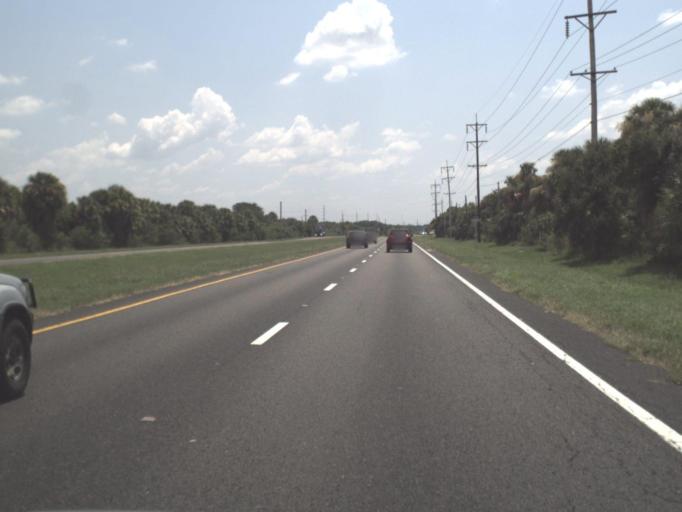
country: US
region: Florida
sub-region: Hillsborough County
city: Gibsonton
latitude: 27.8716
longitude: -82.3891
